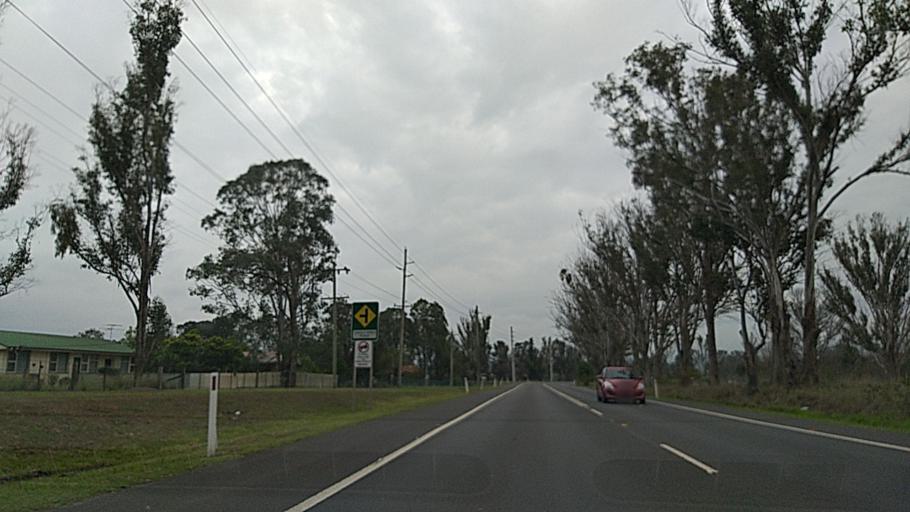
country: AU
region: New South Wales
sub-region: Penrith Municipality
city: Glenmore Park
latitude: -33.8229
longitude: 150.6846
